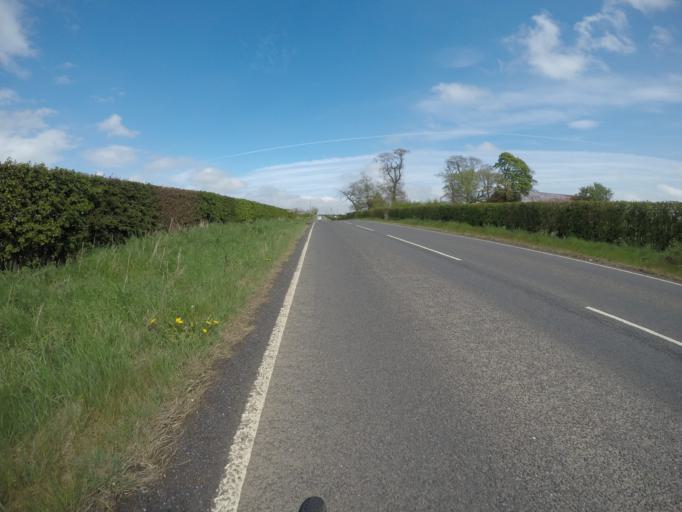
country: GB
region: Scotland
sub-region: East Ayrshire
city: Kilmaurs
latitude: 55.6596
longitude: -4.5515
